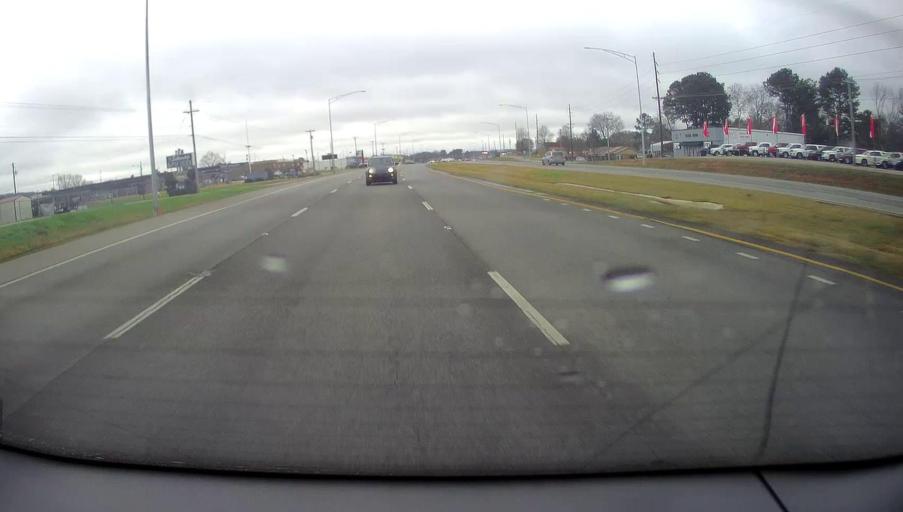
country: US
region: Alabama
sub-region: Morgan County
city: Flint City
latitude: 34.5599
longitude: -86.9922
